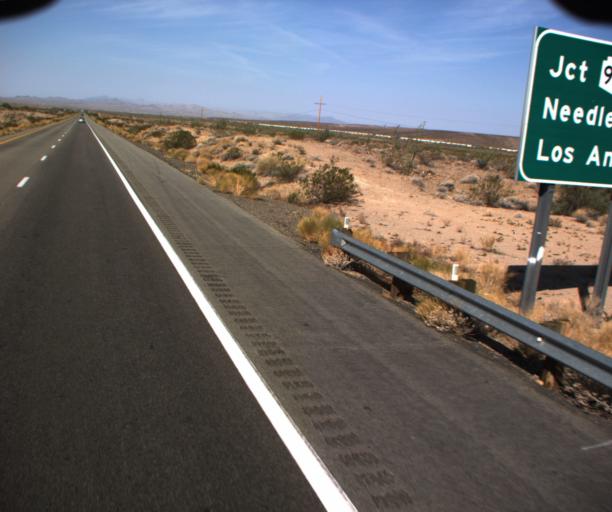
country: US
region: Arizona
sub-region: Mohave County
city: Desert Hills
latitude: 34.7877
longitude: -114.1711
